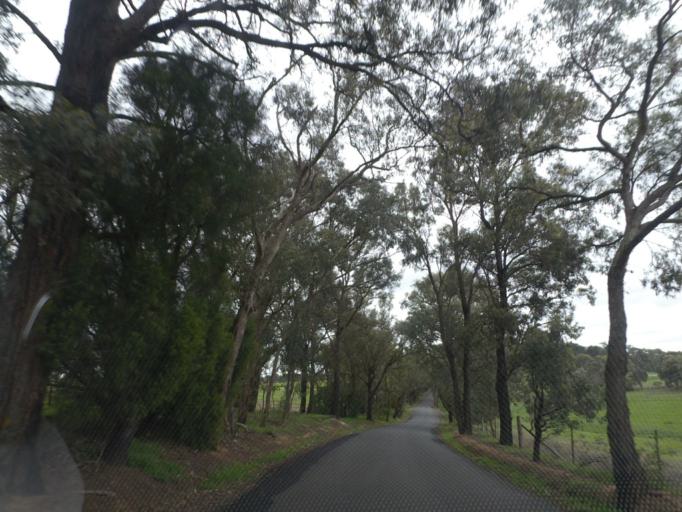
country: AU
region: Victoria
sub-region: Nillumbik
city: Wattleglen
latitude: -37.6666
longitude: 145.2155
